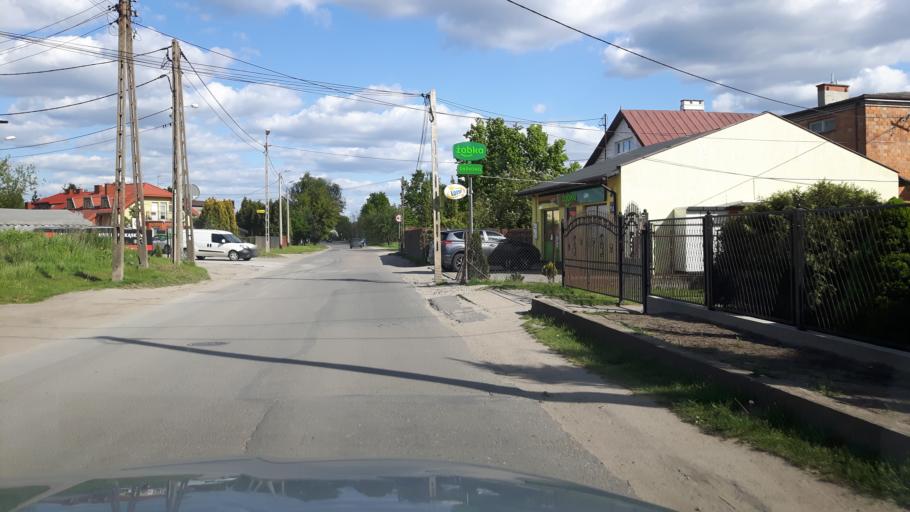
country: PL
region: Masovian Voivodeship
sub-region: Powiat wolominski
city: Marki
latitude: 52.3192
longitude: 21.1218
